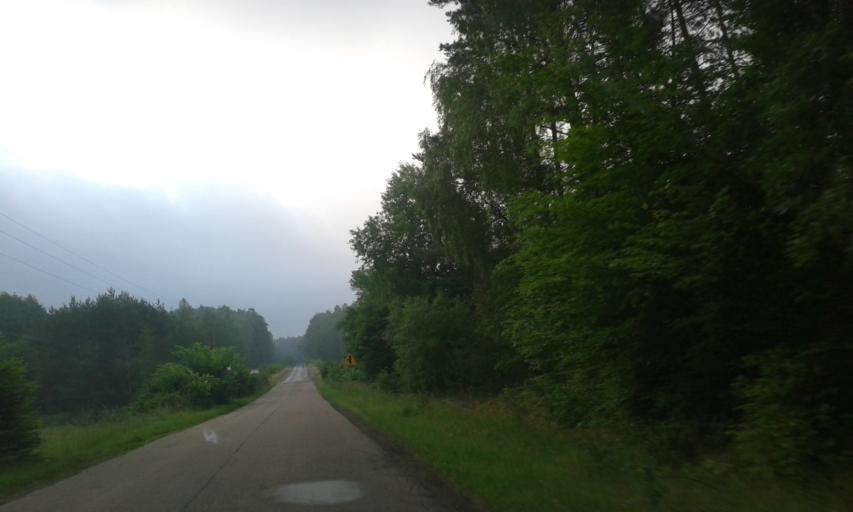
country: PL
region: Kujawsko-Pomorskie
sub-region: Powiat sepolenski
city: Sypniewo
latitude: 53.4546
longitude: 17.3476
